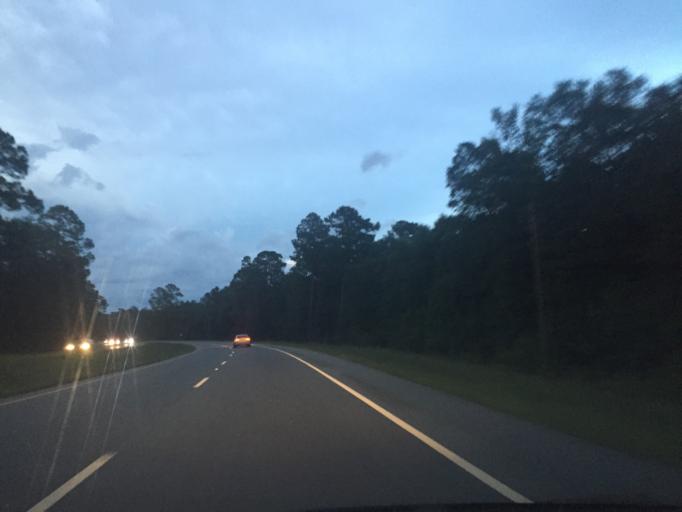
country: US
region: Georgia
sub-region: Liberty County
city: Midway
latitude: 31.8512
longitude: -81.4587
